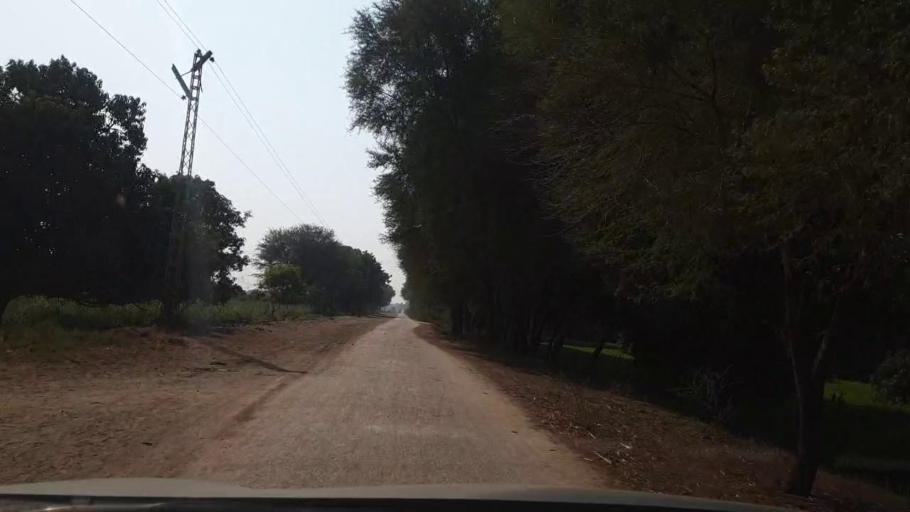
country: PK
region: Sindh
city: Tando Allahyar
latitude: 25.5087
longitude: 68.7861
